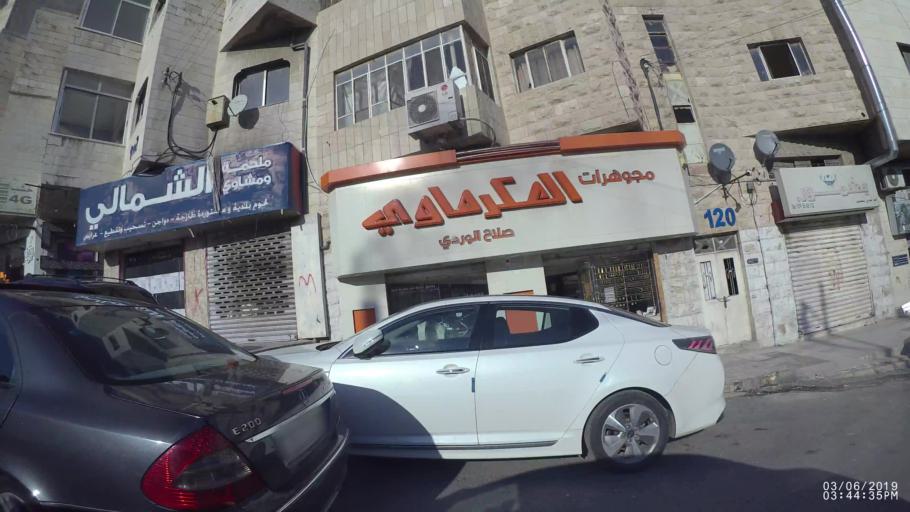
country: JO
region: Amman
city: Amman
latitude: 31.9697
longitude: 35.9593
